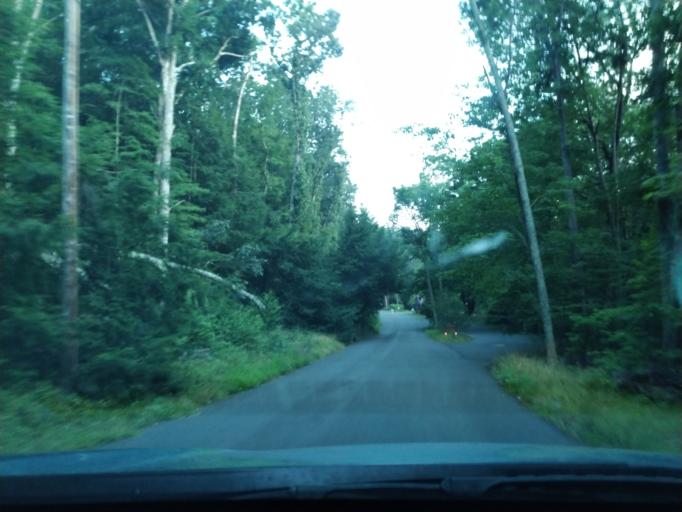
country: US
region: Connecticut
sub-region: New Haven County
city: Southbury
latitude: 41.4229
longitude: -73.2055
